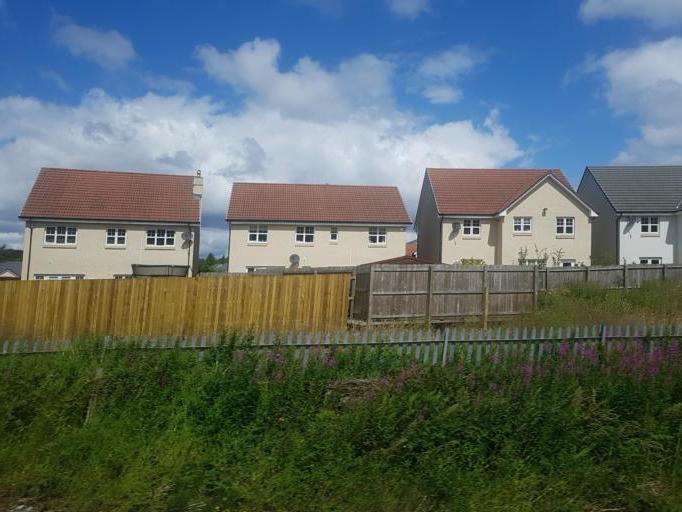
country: GB
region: Scotland
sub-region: Falkirk
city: Falkirk
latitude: 55.9839
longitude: -3.7576
